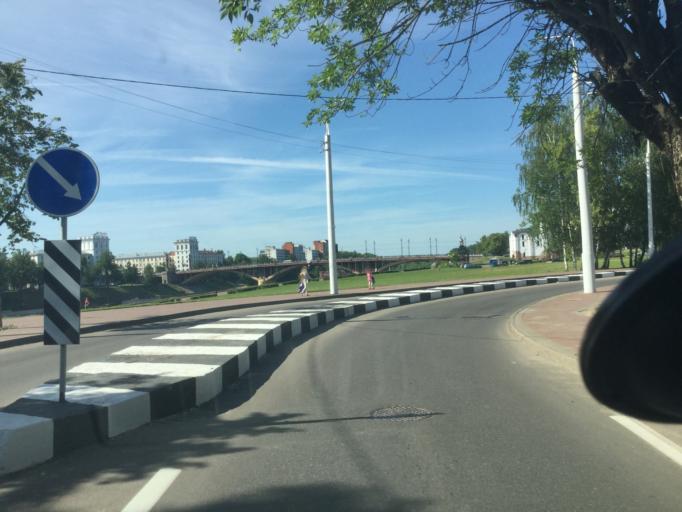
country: BY
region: Vitebsk
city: Vitebsk
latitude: 55.1897
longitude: 30.2004
